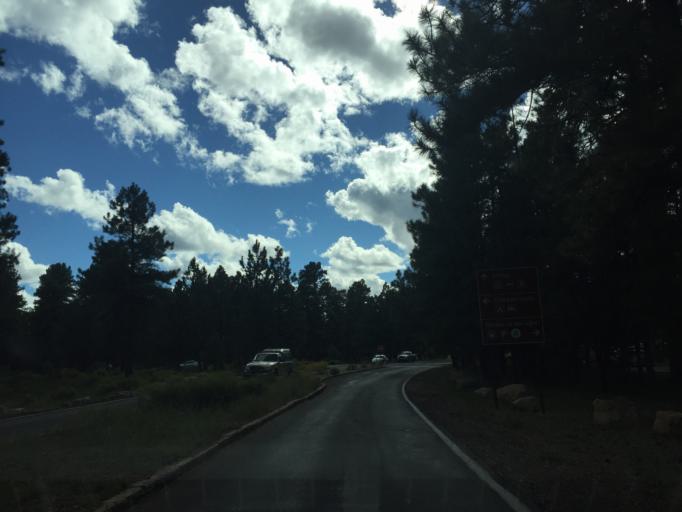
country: US
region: Arizona
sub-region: Coconino County
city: Grand Canyon
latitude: 36.0541
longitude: -112.1223
